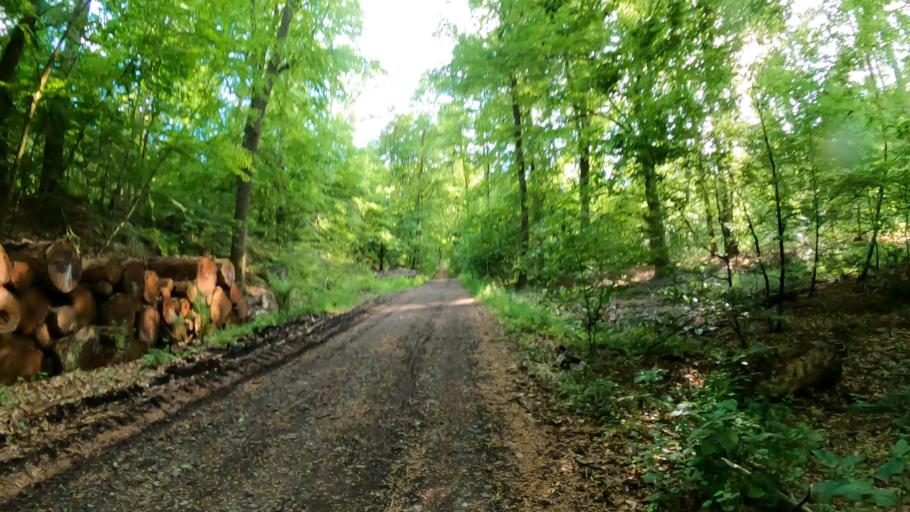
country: DE
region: Lower Saxony
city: Seevetal
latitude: 53.3871
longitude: 9.9432
